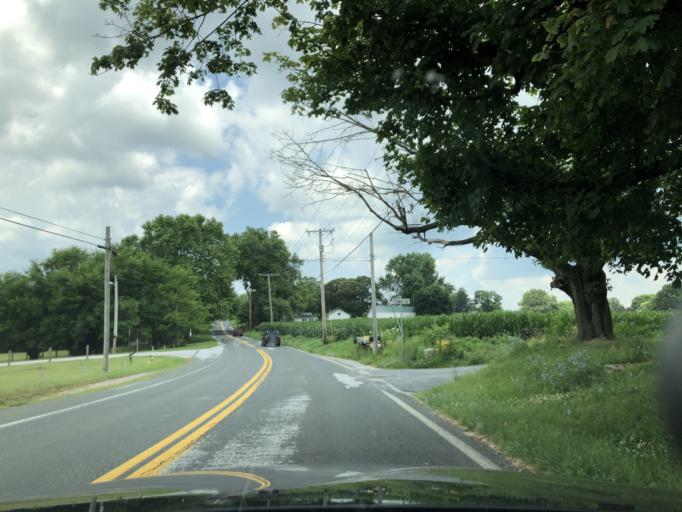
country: US
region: Maryland
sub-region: Carroll County
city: Westminster
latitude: 39.5442
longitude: -76.9894
